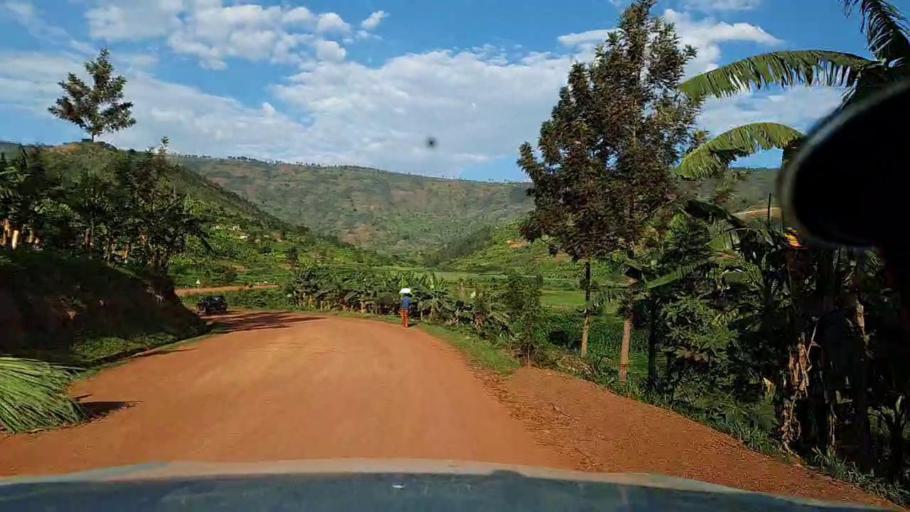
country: RW
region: Kigali
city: Kigali
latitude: -1.8649
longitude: 29.9280
